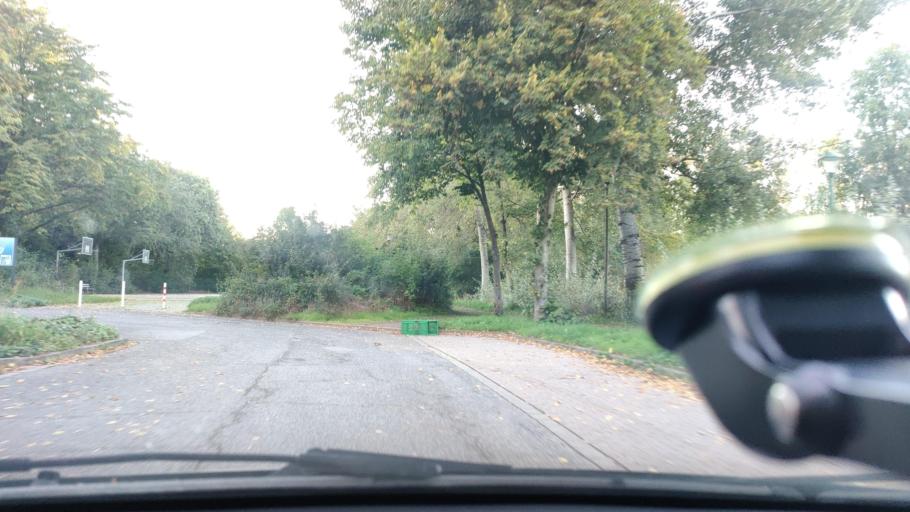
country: DE
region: North Rhine-Westphalia
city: Kalkar
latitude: 51.7402
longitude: 6.2970
